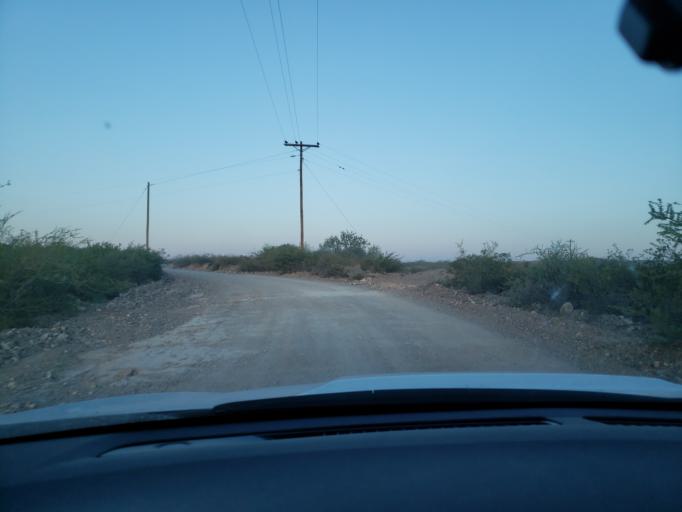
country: US
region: Texas
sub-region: Culberson County
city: Van Horn
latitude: 30.7235
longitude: -104.7548
